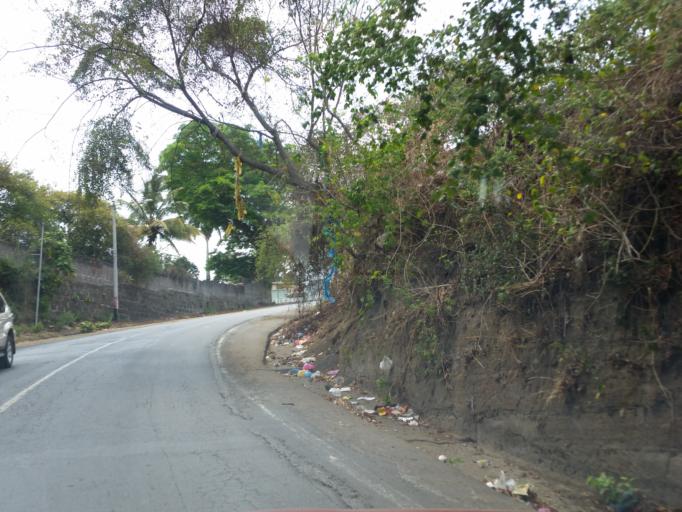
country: NI
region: Managua
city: Managua
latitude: 12.0860
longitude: -86.2416
